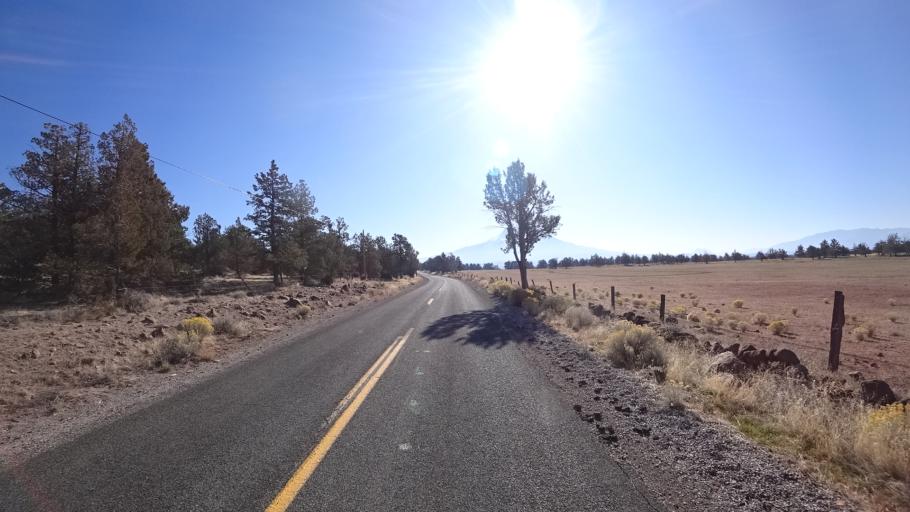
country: US
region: California
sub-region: Siskiyou County
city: Weed
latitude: 41.6294
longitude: -122.3332
